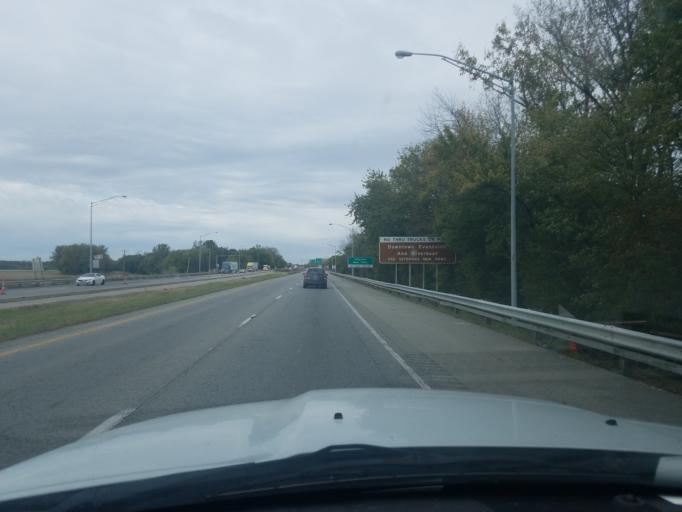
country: US
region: Indiana
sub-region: Vanderburgh County
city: Evansville
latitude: 37.9272
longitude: -87.5481
